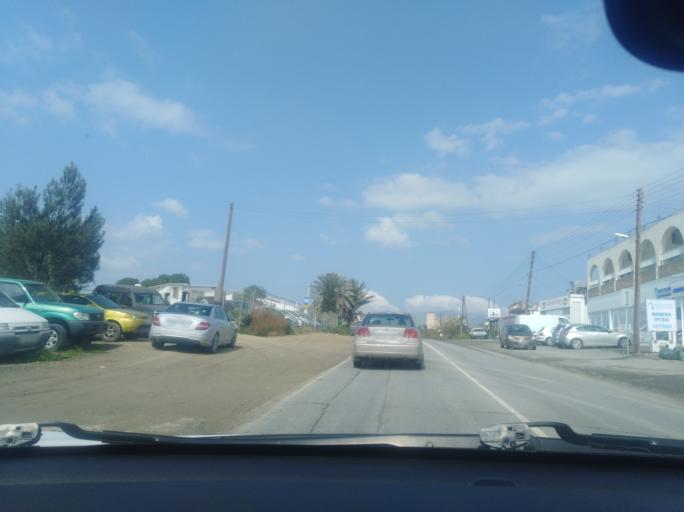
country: CY
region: Lefkosia
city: Nicosia
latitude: 35.1686
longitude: 33.3980
